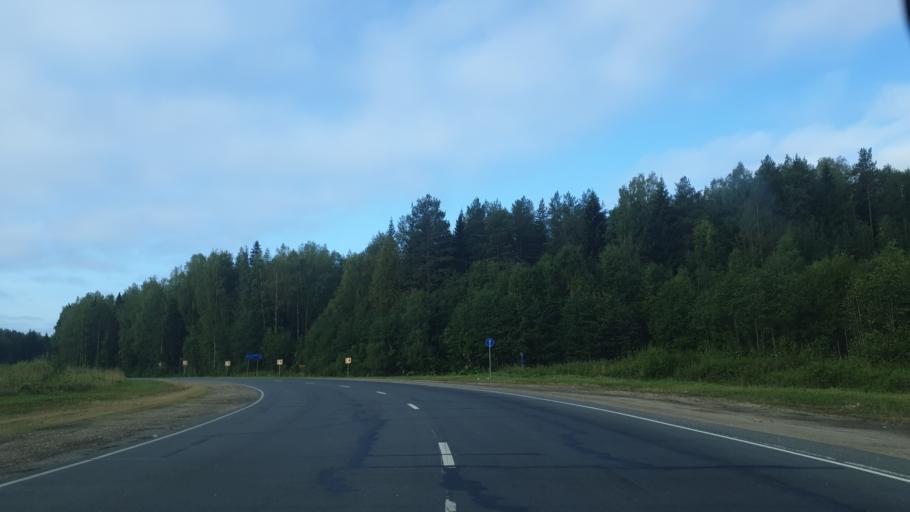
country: RU
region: Komi Republic
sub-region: Syktyvdinskiy Rayon
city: Syktyvkar
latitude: 61.5594
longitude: 50.6339
